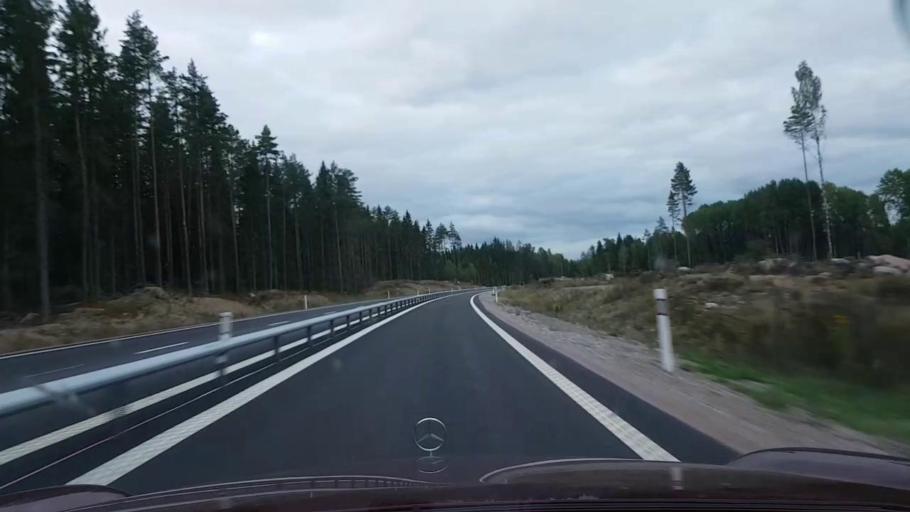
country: SE
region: Vaestmanland
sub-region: Hallstahammars Kommun
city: Hallstahammar
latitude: 59.6579
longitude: 16.2043
